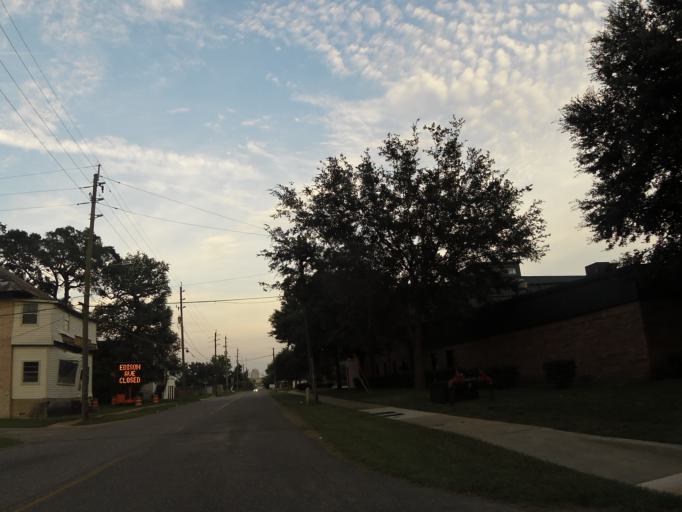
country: US
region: Florida
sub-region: Duval County
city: Jacksonville
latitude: 30.3260
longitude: -81.6878
